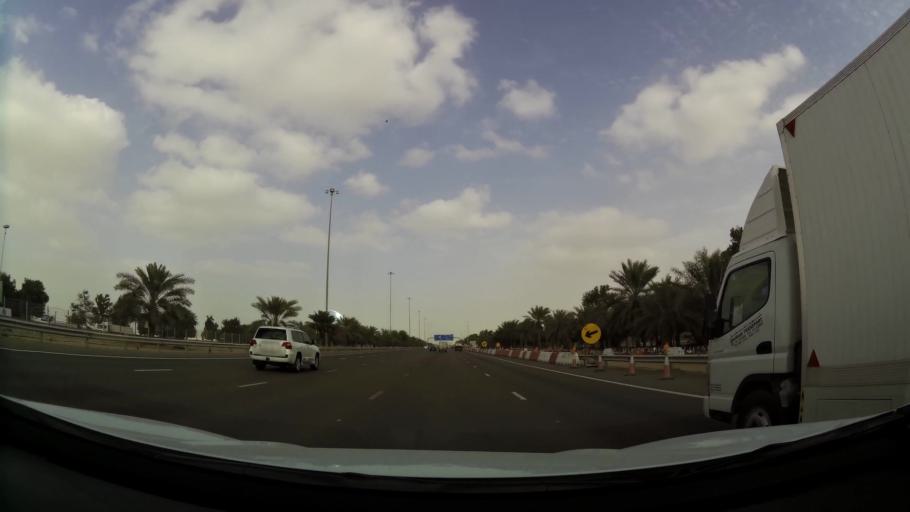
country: AE
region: Abu Dhabi
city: Abu Dhabi
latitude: 24.4345
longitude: 54.5634
